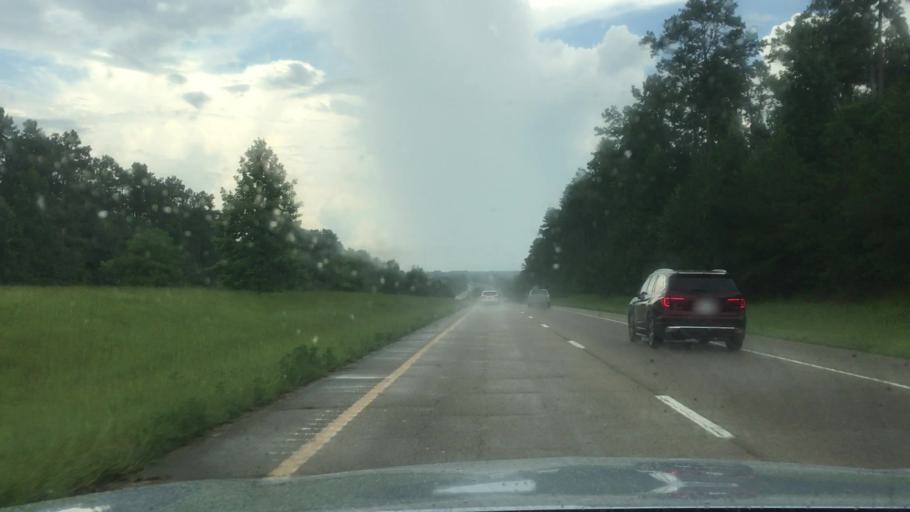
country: US
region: Mississippi
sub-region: Lamar County
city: Purvis
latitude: 31.1584
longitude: -89.3579
